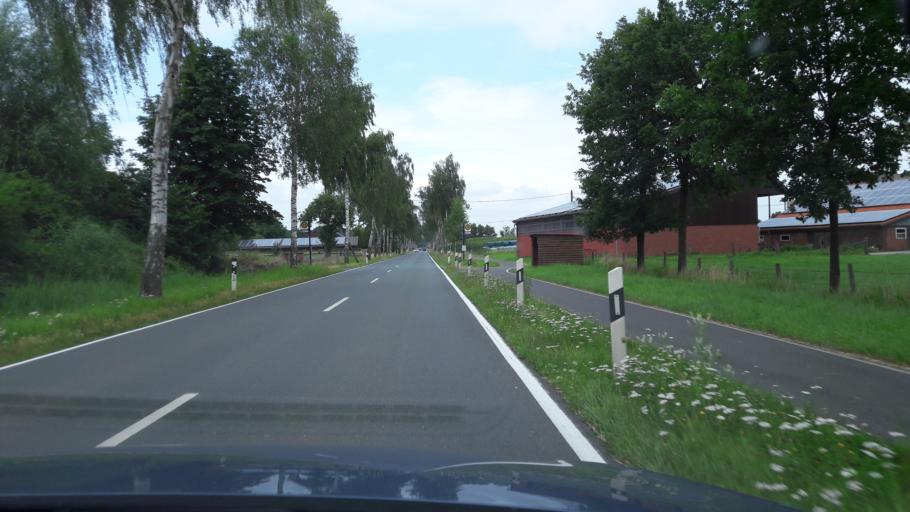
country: DE
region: North Rhine-Westphalia
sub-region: Regierungsbezirk Munster
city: Everswinkel
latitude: 51.8861
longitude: 7.8911
